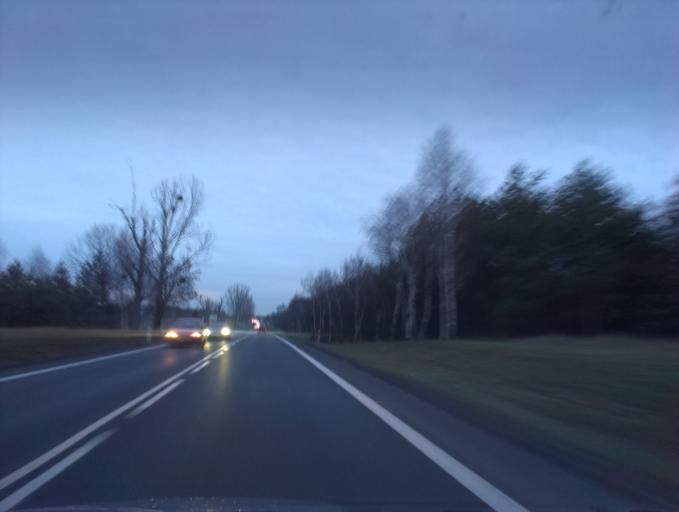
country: PL
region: Greater Poland Voivodeship
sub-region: Powiat poznanski
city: Zlotniki
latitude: 52.5385
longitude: 16.8372
